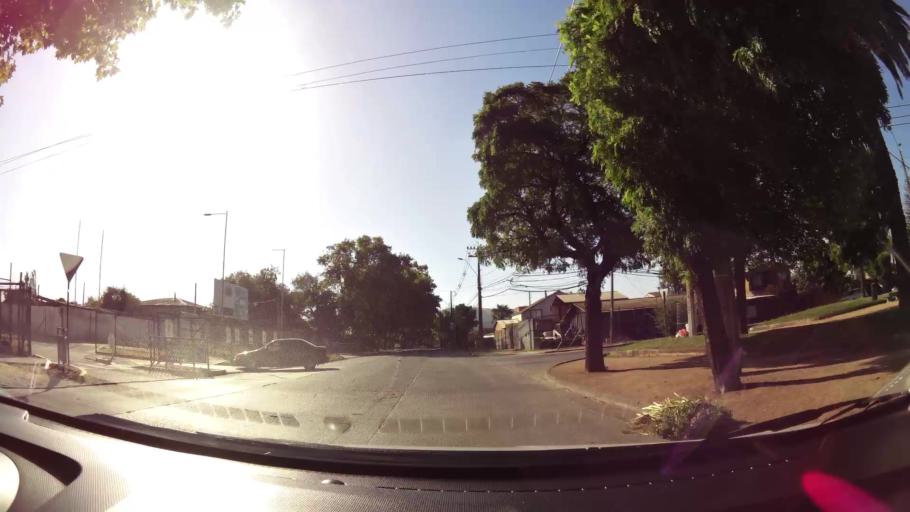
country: CL
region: Maule
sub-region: Provincia de Talca
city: Talca
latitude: -35.4349
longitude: -71.6663
